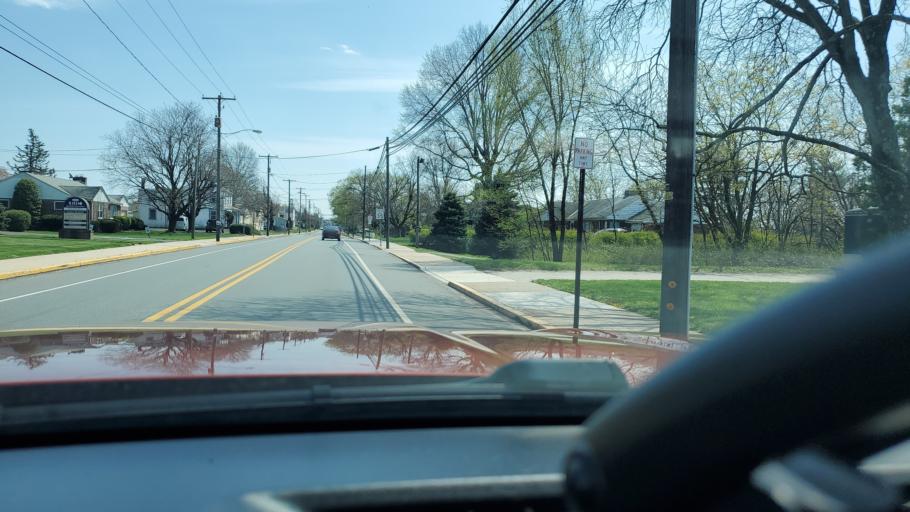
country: US
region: Pennsylvania
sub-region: Montgomery County
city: Pennsburg
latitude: 40.3833
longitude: -75.4871
